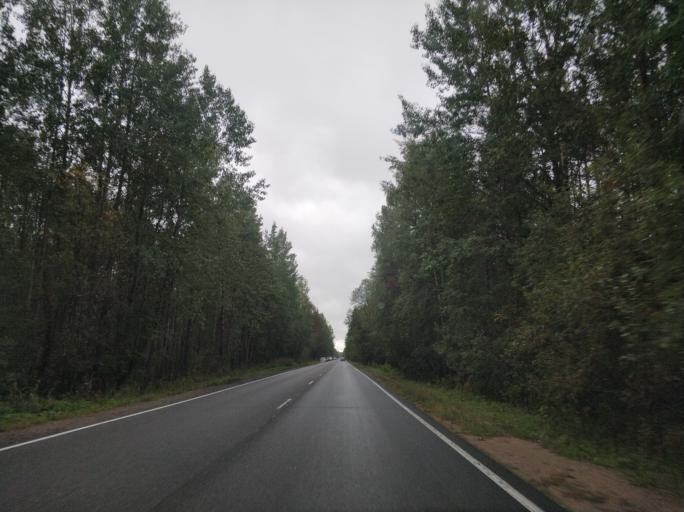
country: RU
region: Leningrad
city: Borisova Griva
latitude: 60.1485
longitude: 30.9404
